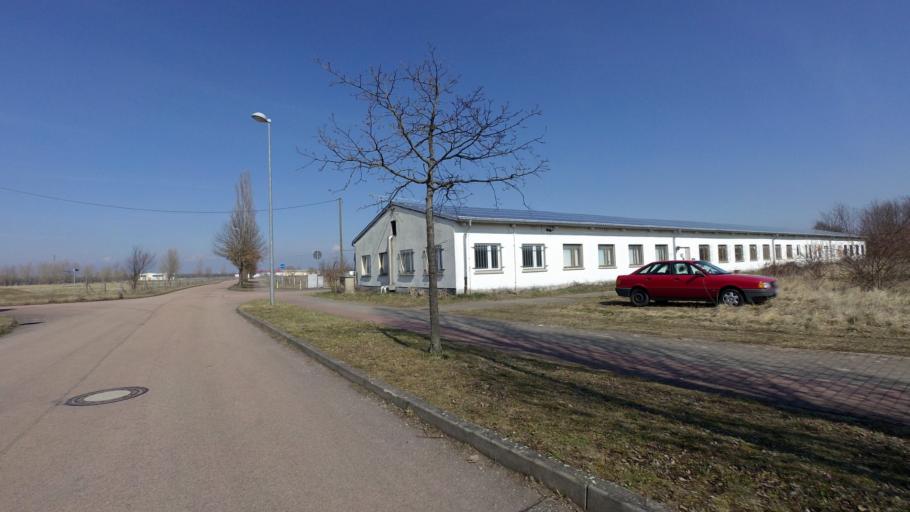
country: DE
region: Saxony-Anhalt
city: Vockerode
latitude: 51.8475
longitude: 12.3439
